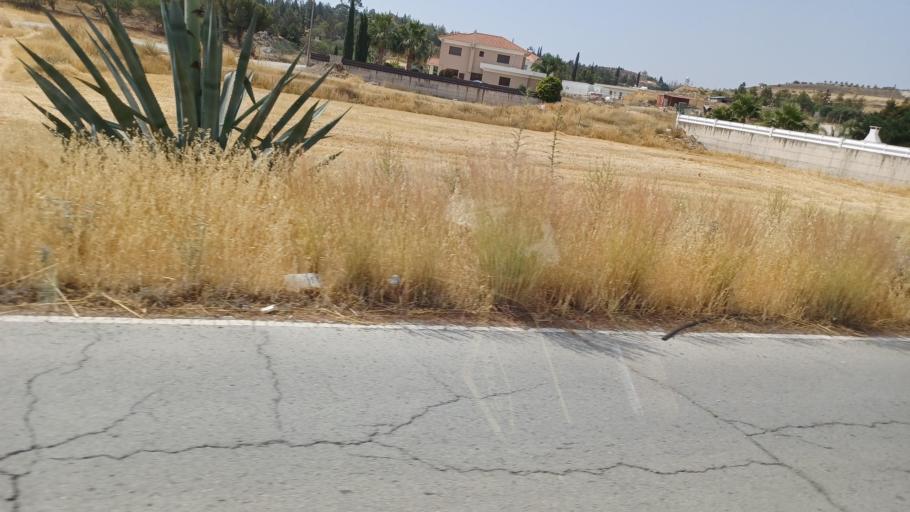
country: CY
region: Larnaka
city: Aradippou
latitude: 34.9464
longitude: 33.5677
